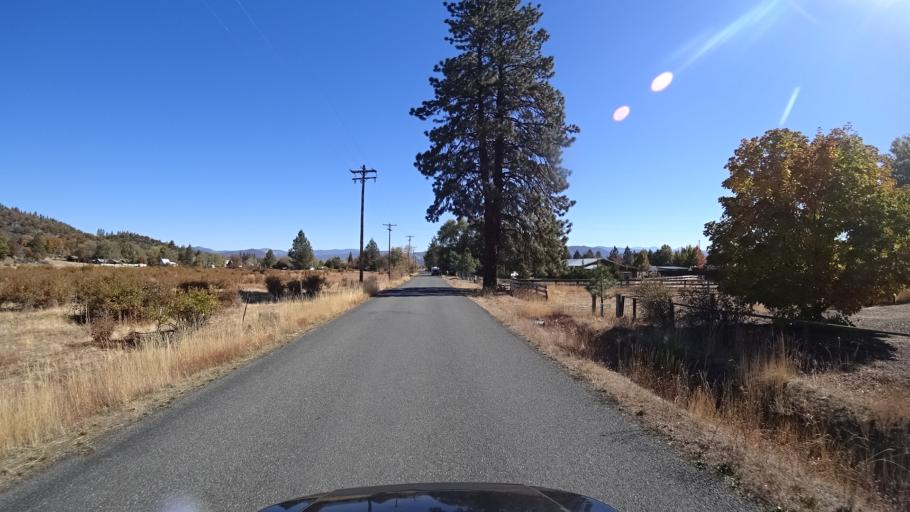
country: US
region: California
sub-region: Siskiyou County
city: Yreka
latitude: 41.5485
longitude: -122.9128
